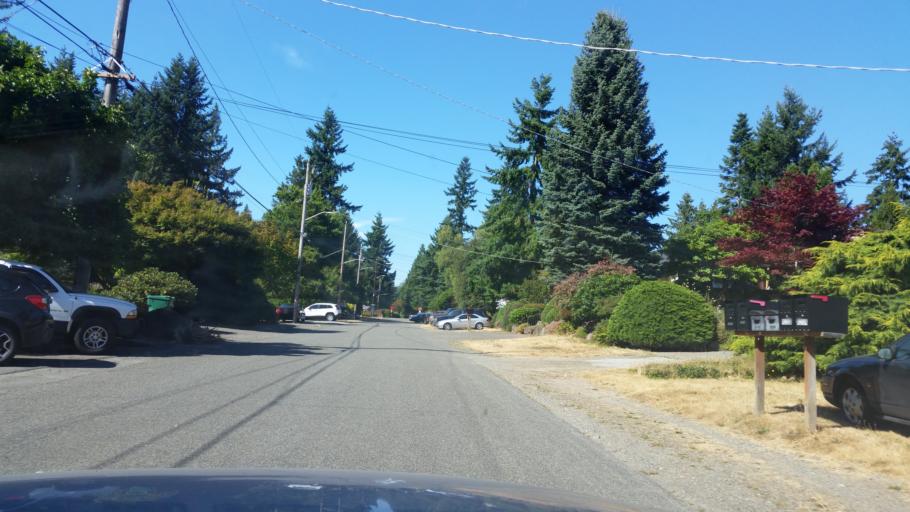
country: US
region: Washington
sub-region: King County
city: Shoreline
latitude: 47.7217
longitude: -122.3596
